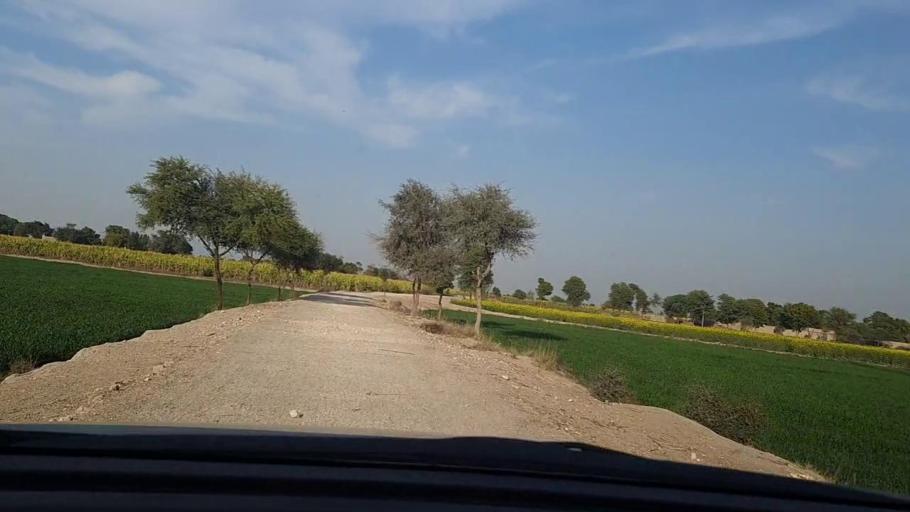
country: PK
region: Sindh
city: Daulatpur
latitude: 26.3302
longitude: 68.0276
